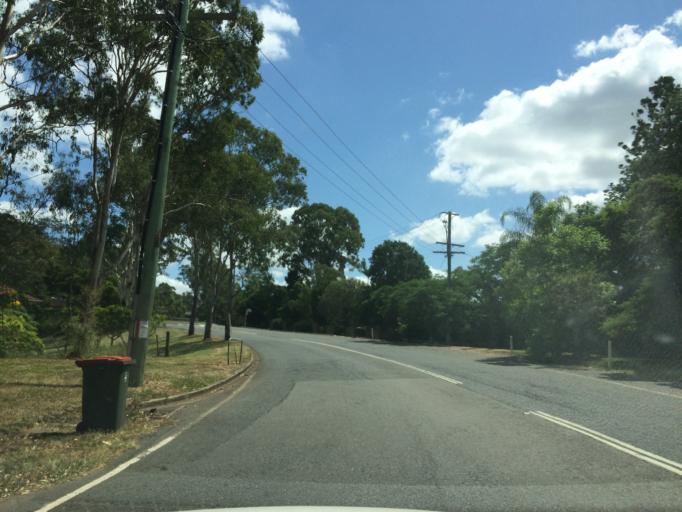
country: AU
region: Queensland
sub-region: Brisbane
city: Kenmore Hills
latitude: -27.4975
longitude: 152.9283
